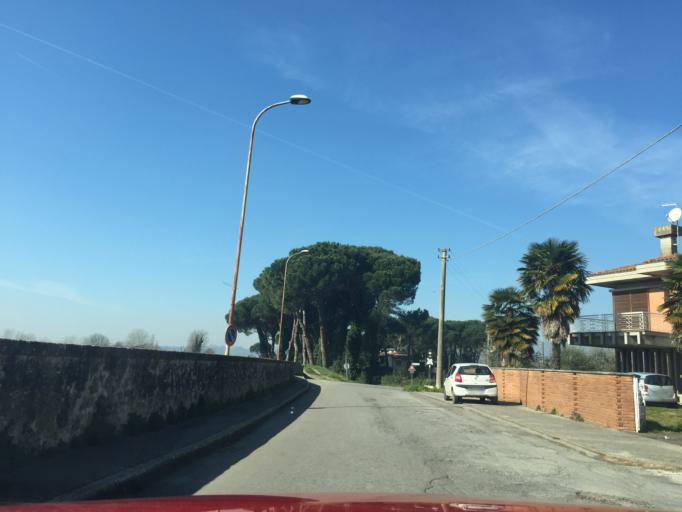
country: IT
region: Tuscany
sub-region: Provincia di Pistoia
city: Ponte Buggianese
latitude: 43.8422
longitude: 10.7447
